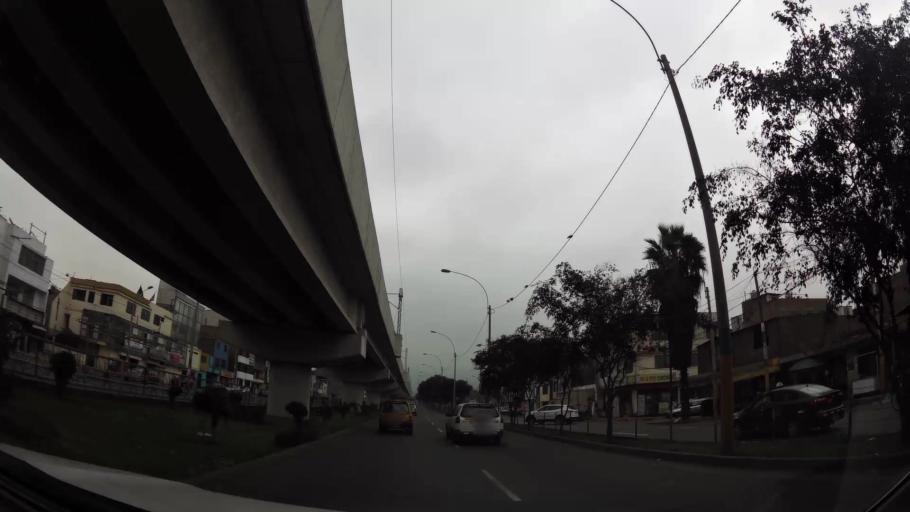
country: PE
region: Lima
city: Lima
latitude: -12.0254
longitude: -77.0098
